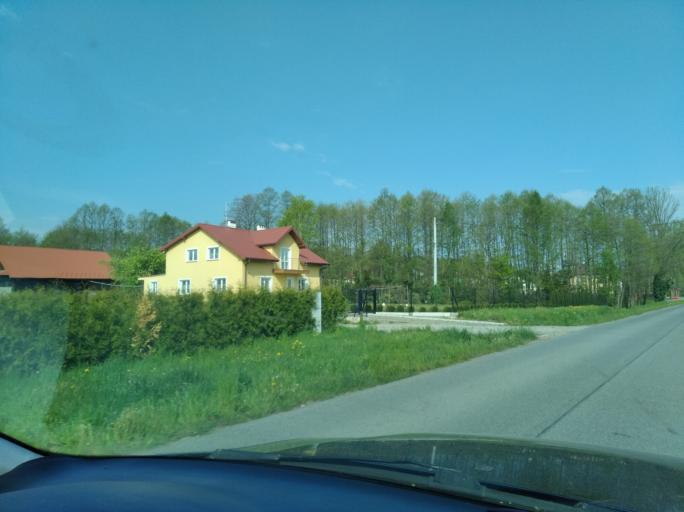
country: PL
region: Subcarpathian Voivodeship
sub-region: Powiat brzozowski
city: Nozdrzec
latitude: 49.7646
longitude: 22.2154
